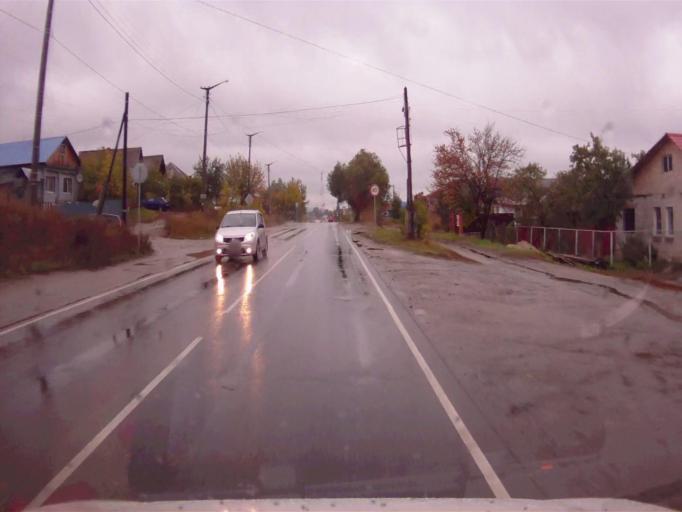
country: RU
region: Chelyabinsk
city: Kyshtym
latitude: 55.7121
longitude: 60.5579
